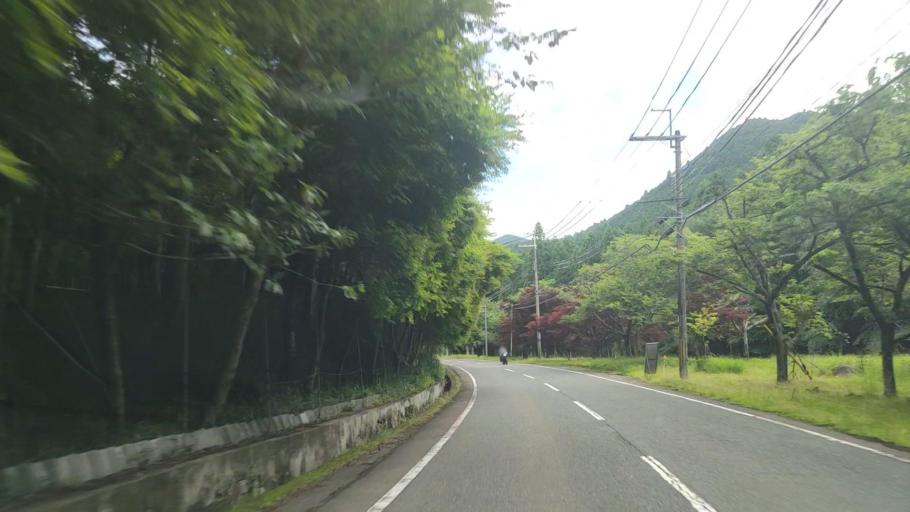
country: JP
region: Kyoto
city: Fukuchiyama
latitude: 35.1929
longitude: 134.9334
